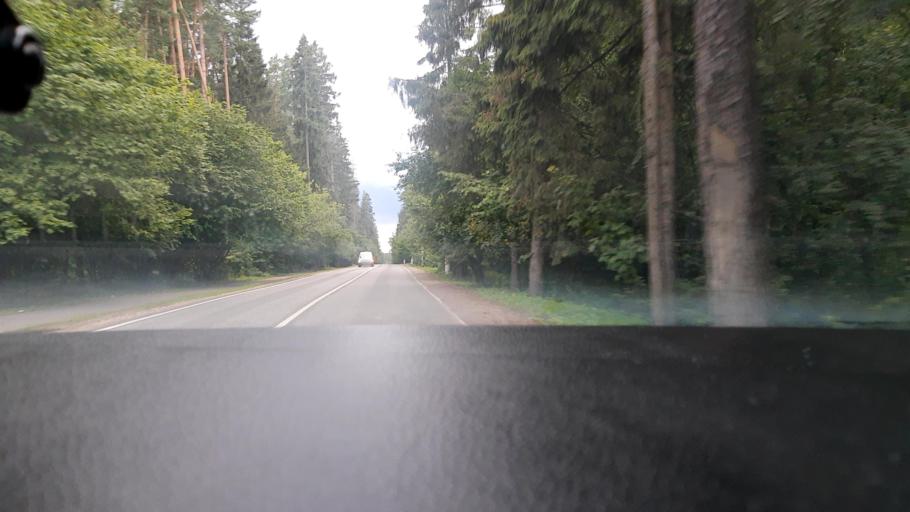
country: RU
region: Moskovskaya
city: Lesnoy Gorodok
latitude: 55.6778
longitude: 37.1871
